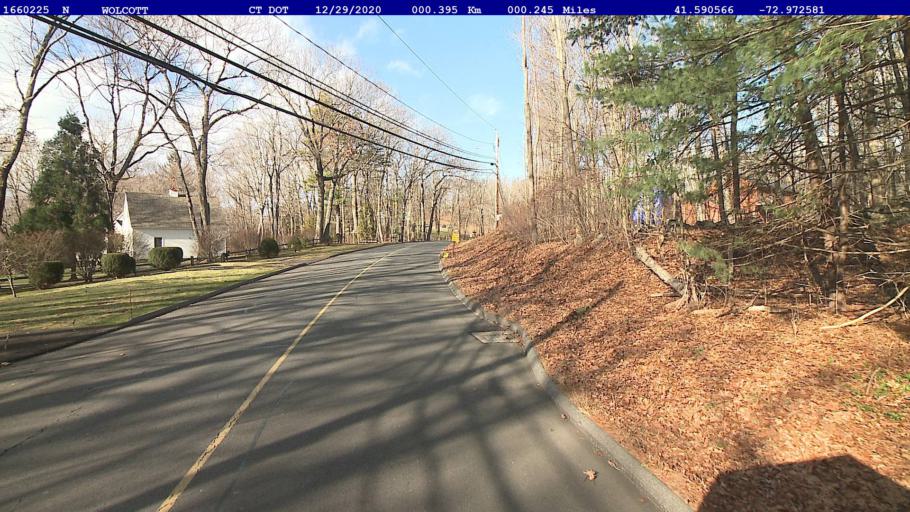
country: US
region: Connecticut
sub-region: New Haven County
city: Wolcott
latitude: 41.5908
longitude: -72.9727
